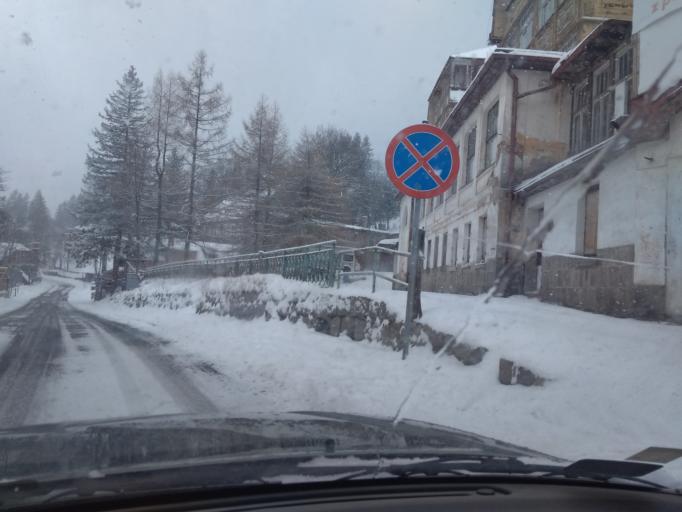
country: PL
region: Lower Silesian Voivodeship
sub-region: Powiat jeleniogorski
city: Karpacz
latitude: 50.7806
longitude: 15.7246
